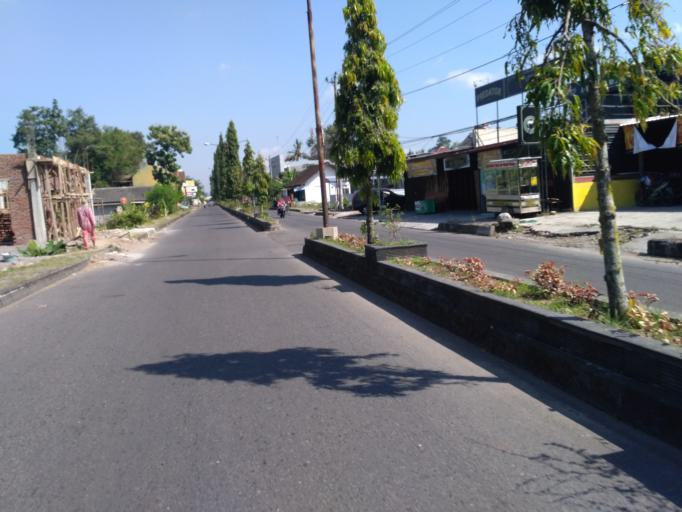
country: ID
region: Daerah Istimewa Yogyakarta
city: Depok
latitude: -7.7514
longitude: 110.4286
